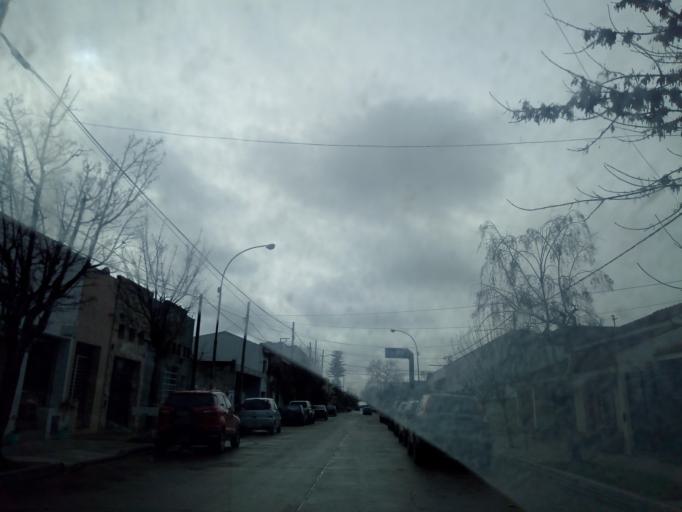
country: AR
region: Buenos Aires
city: Necochea
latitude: -38.5592
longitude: -58.7352
